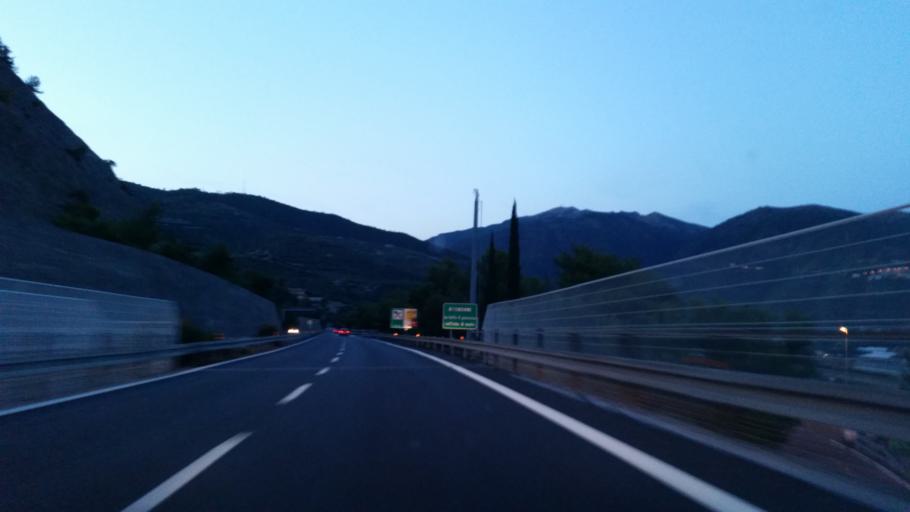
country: IT
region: Liguria
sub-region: Provincia di Imperia
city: Taggia
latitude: 43.8503
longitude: 7.8392
